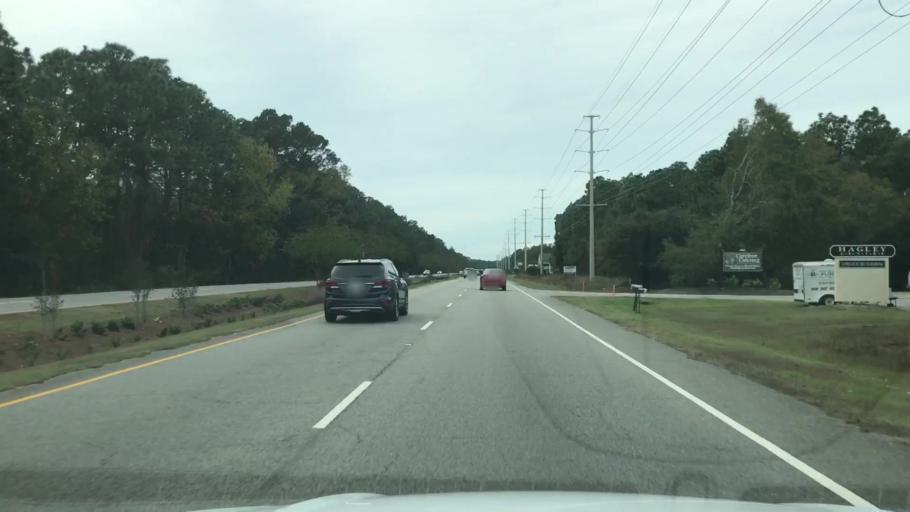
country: US
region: South Carolina
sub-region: Georgetown County
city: Georgetown
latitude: 33.4242
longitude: -79.1629
